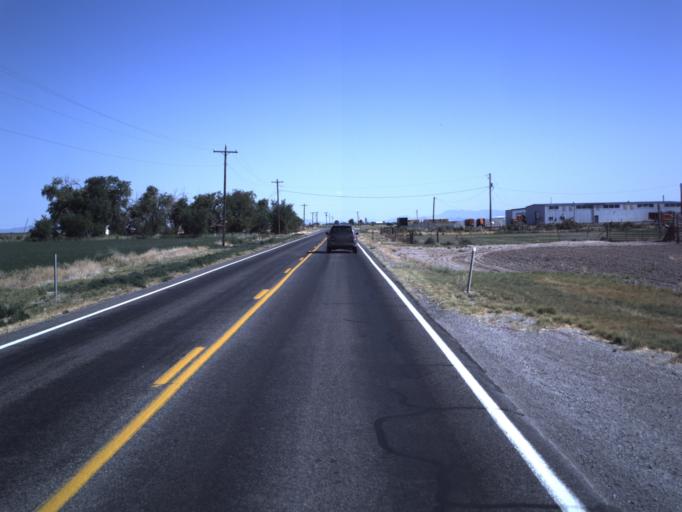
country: US
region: Utah
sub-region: Millard County
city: Delta
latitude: 39.3254
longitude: -112.6523
